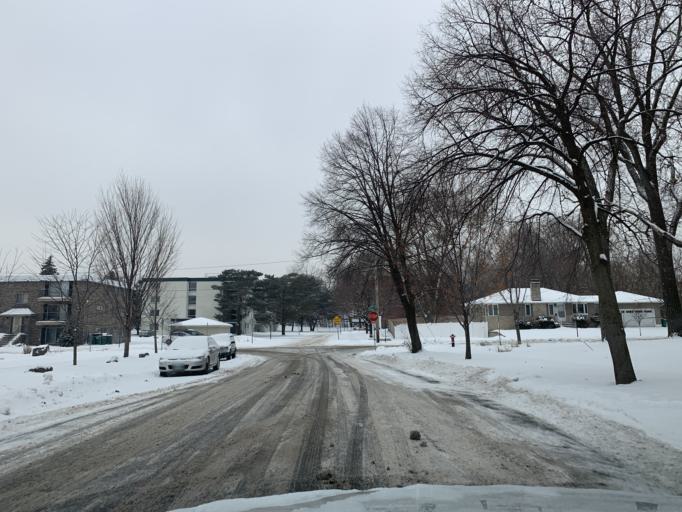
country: US
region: Minnesota
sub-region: Hennepin County
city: Saint Louis Park
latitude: 44.9498
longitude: -93.3332
